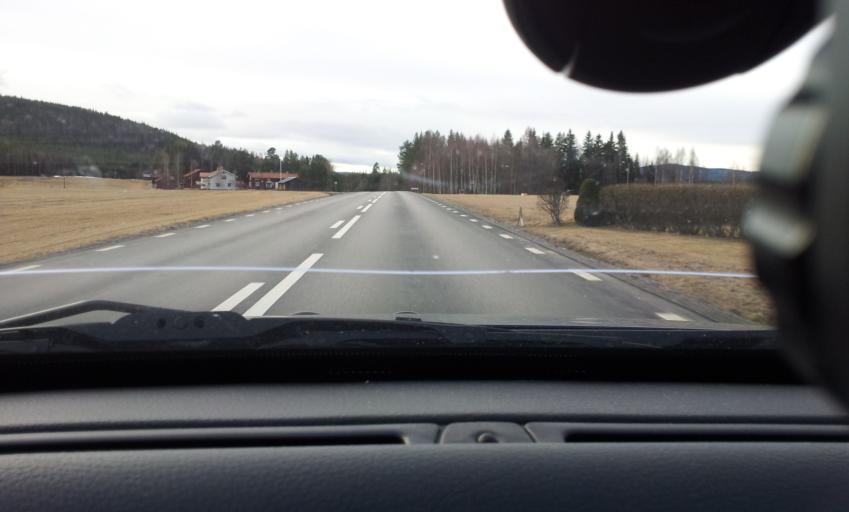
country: SE
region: Gaevleborg
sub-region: Ljusdals Kommun
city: Farila
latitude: 61.8748
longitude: 15.7218
